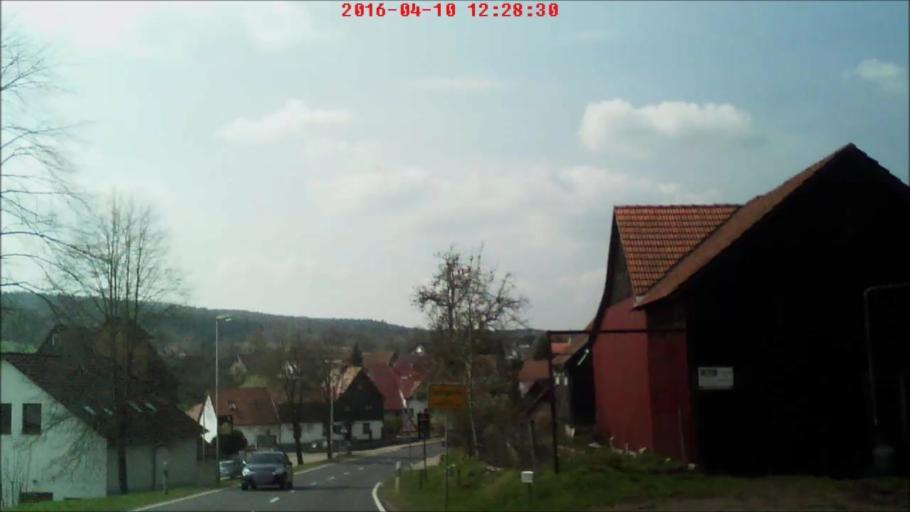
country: DE
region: Thuringia
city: Springstille
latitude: 50.6858
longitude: 10.5324
